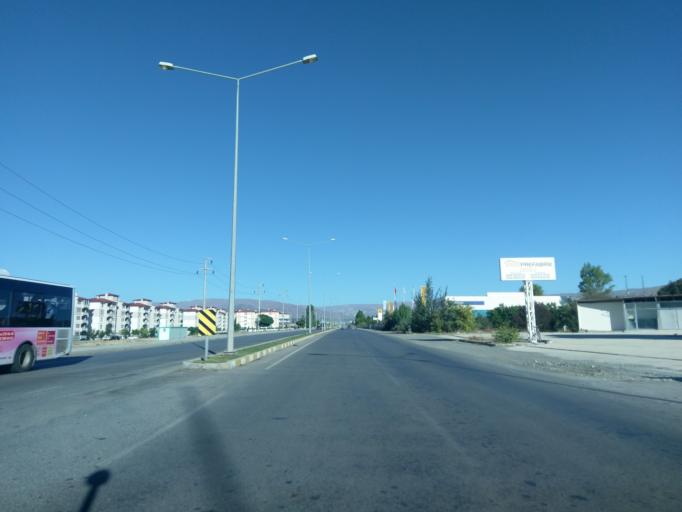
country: TR
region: Erzincan
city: Erzincan
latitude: 39.7564
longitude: 39.4489
